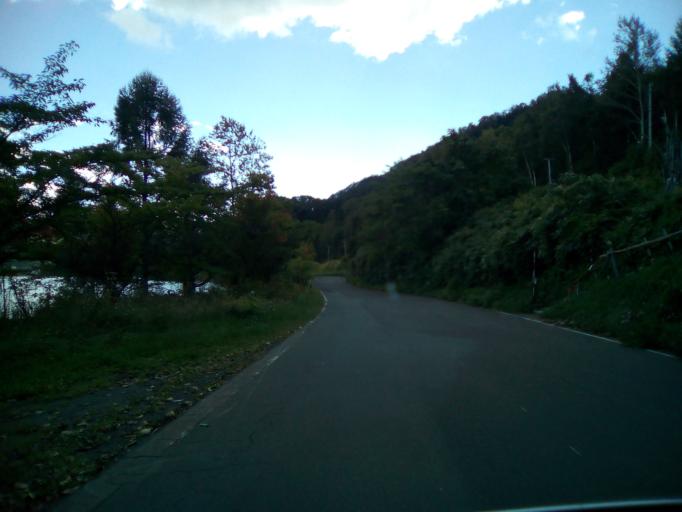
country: JP
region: Hokkaido
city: Date
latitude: 42.5834
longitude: 140.7955
